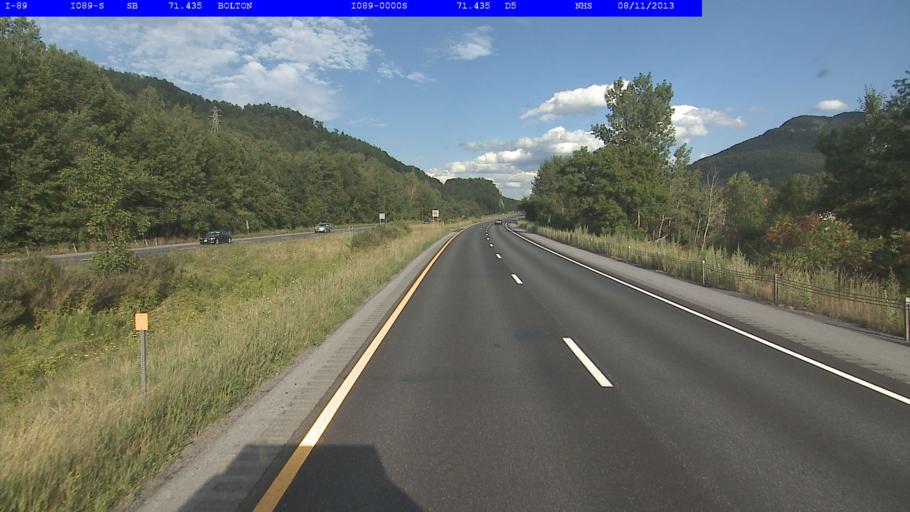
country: US
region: Vermont
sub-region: Washington County
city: Waterbury
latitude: 44.3776
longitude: -72.8952
